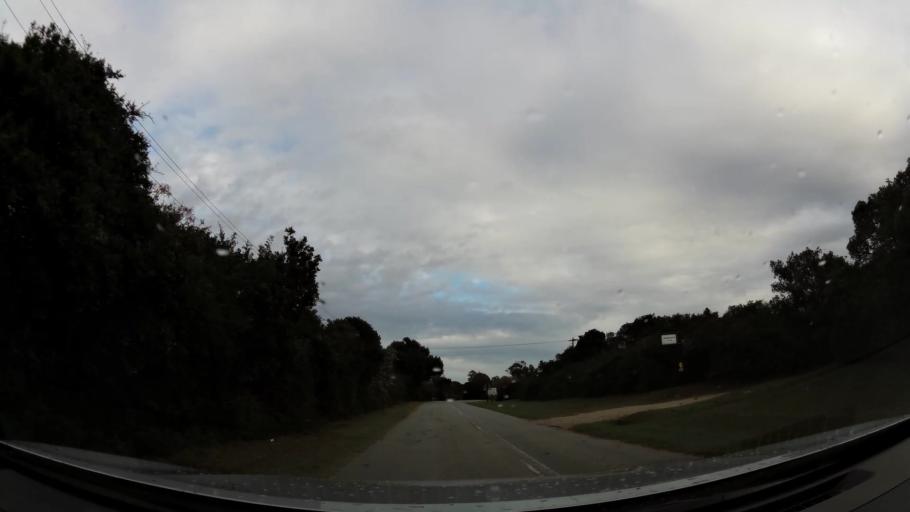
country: ZA
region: Eastern Cape
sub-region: Nelson Mandela Bay Metropolitan Municipality
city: Port Elizabeth
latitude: -34.0162
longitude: 25.5066
